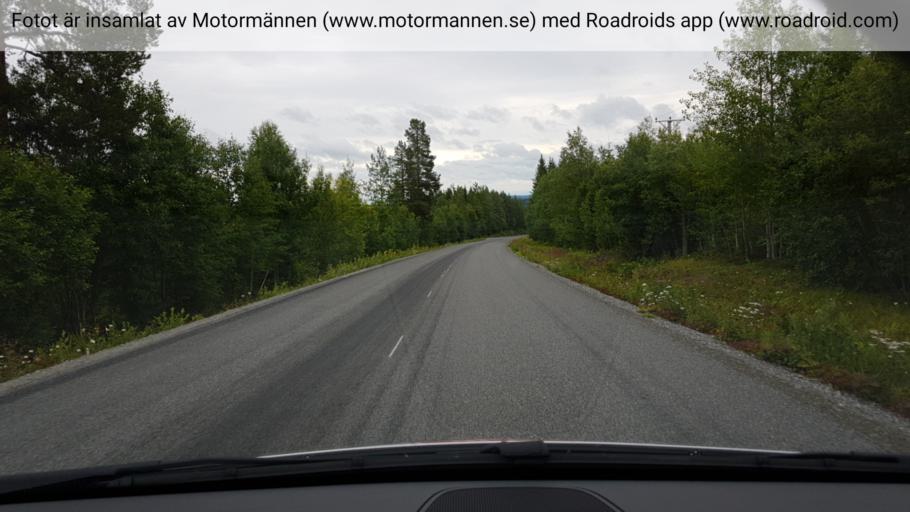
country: SE
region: Jaemtland
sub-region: Krokoms Kommun
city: Krokom
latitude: 63.6684
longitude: 14.5355
